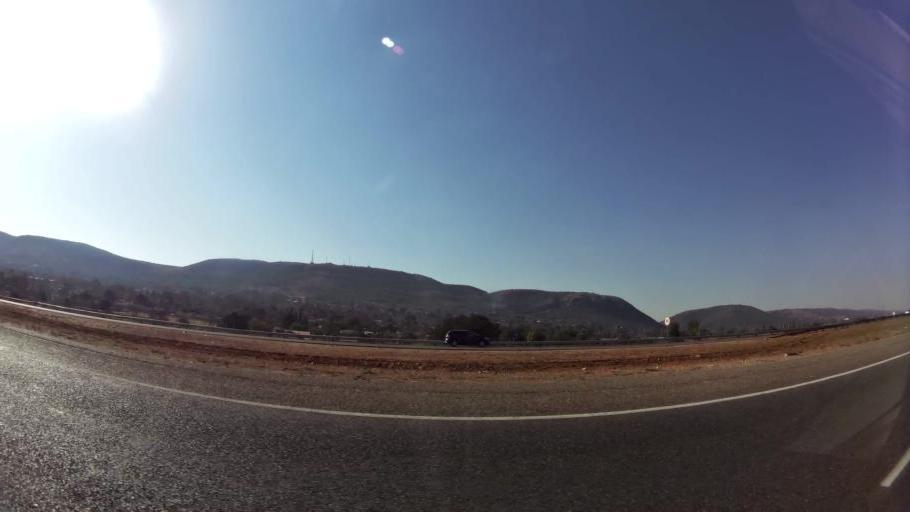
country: ZA
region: Gauteng
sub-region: City of Tshwane Metropolitan Municipality
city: Pretoria
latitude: -25.7072
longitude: 28.1651
